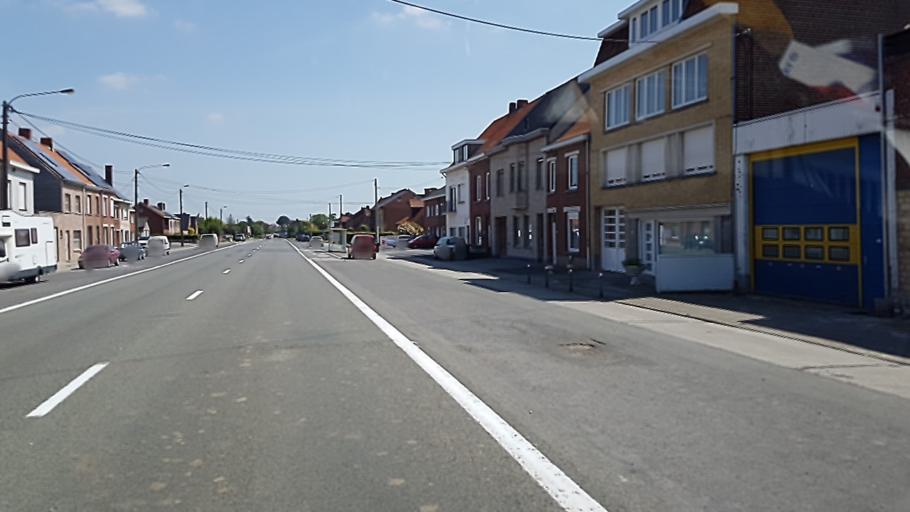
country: BE
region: Flanders
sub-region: Provincie West-Vlaanderen
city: Wervik
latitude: 50.8135
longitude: 3.0631
